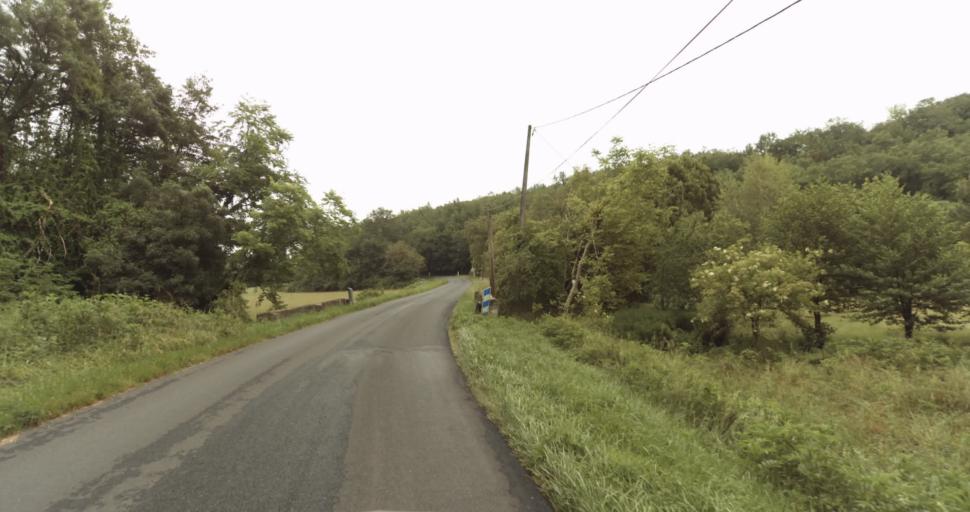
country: FR
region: Aquitaine
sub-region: Departement de la Dordogne
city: Lalinde
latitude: 44.8555
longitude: 0.7748
